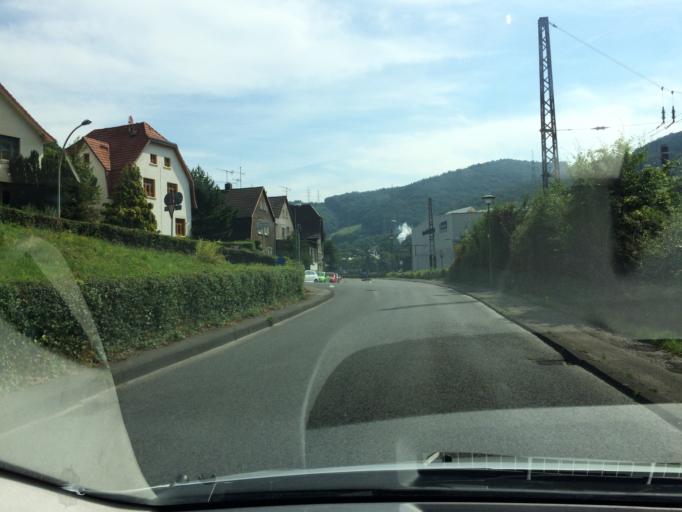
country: DE
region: North Rhine-Westphalia
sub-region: Regierungsbezirk Arnsberg
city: Nachrodt-Wiblingwerde
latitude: 51.3461
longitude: 7.5932
